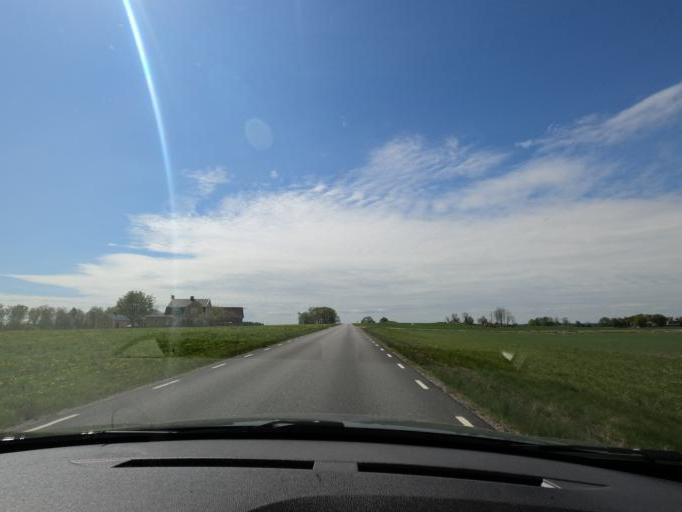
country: SE
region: Joenkoeping
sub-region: Varnamo Kommun
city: Bredaryd
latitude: 57.1461
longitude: 13.7217
